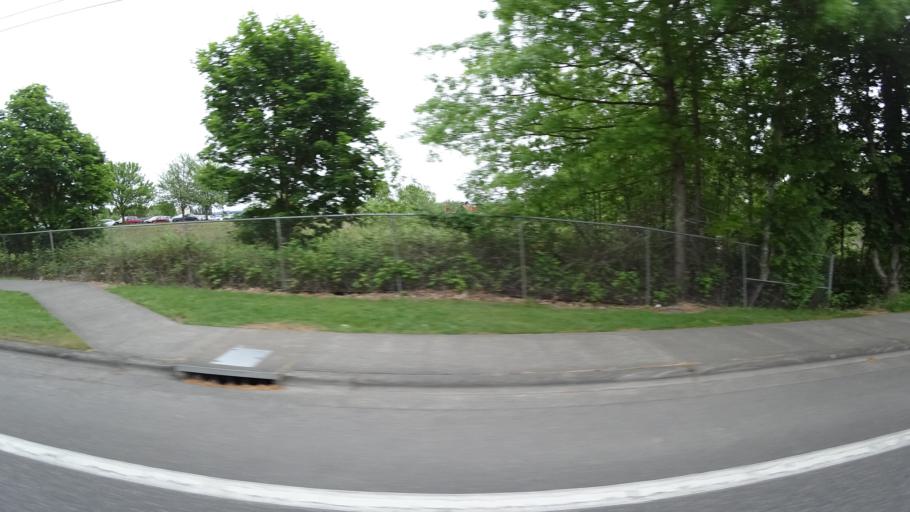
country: US
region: Oregon
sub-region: Washington County
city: Bethany
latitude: 45.5481
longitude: -122.8675
